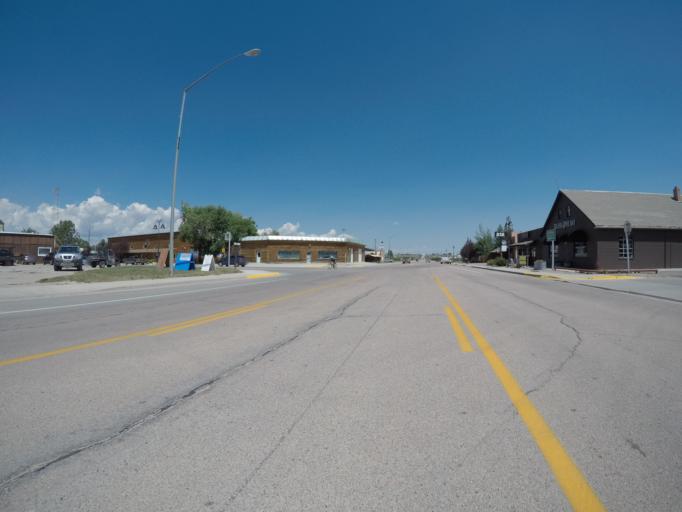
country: US
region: Wyoming
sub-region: Sublette County
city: Marbleton
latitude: 42.5379
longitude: -110.1098
